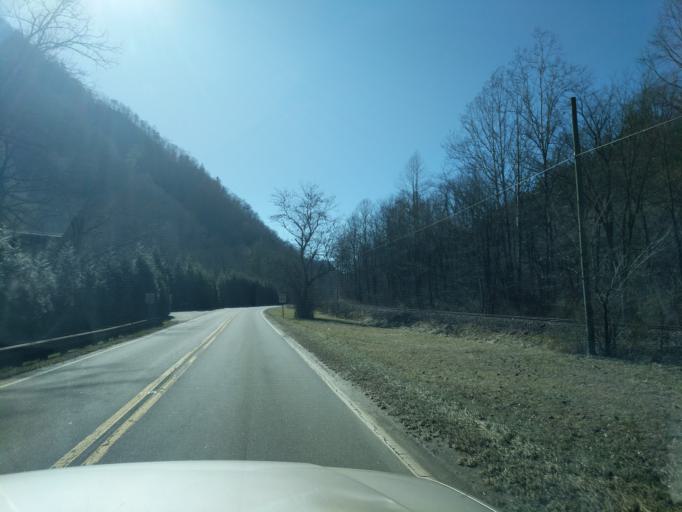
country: US
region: North Carolina
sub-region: Graham County
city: Robbinsville
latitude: 35.3007
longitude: -83.6546
